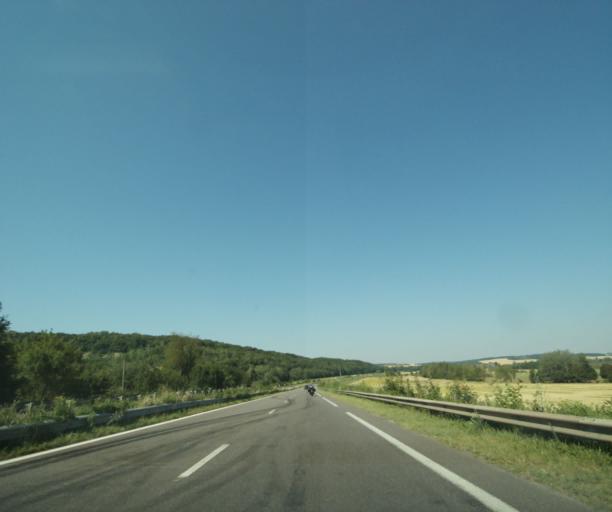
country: FR
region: Lorraine
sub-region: Departement de la Meuse
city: Vacon
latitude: 48.6866
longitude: 5.6594
